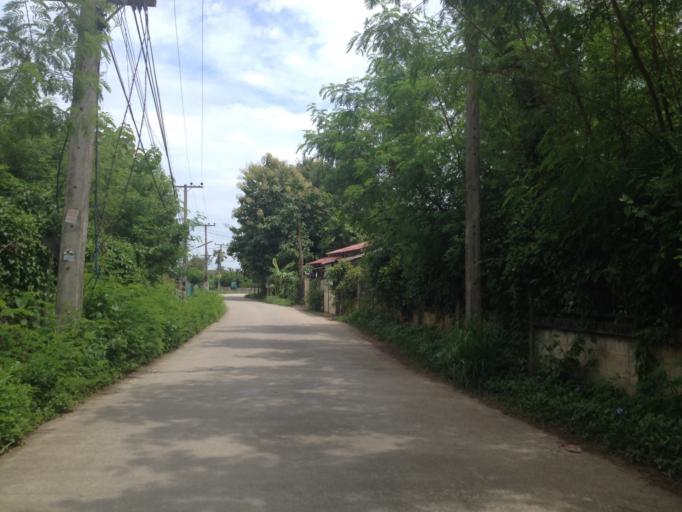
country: TH
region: Chiang Mai
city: Hang Dong
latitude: 18.7023
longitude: 98.9356
